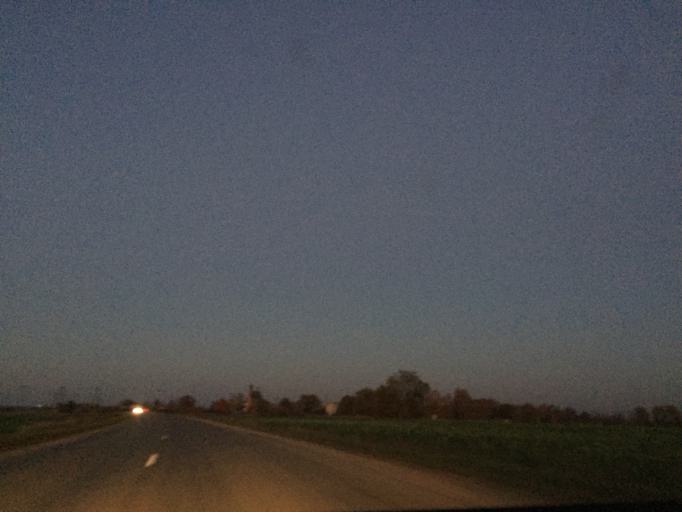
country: LV
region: Tervete
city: Zelmeni
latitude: 56.5004
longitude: 23.2616
